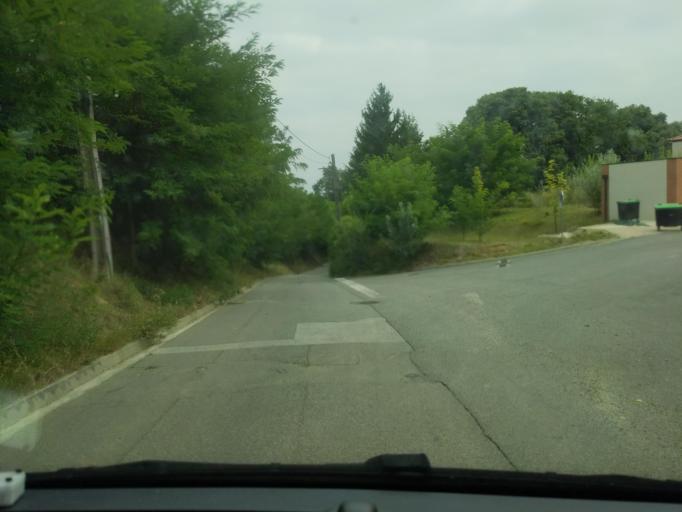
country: FR
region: Midi-Pyrenees
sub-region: Departement de la Haute-Garonne
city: Ramonville-Saint-Agne
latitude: 43.5500
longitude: 1.4602
